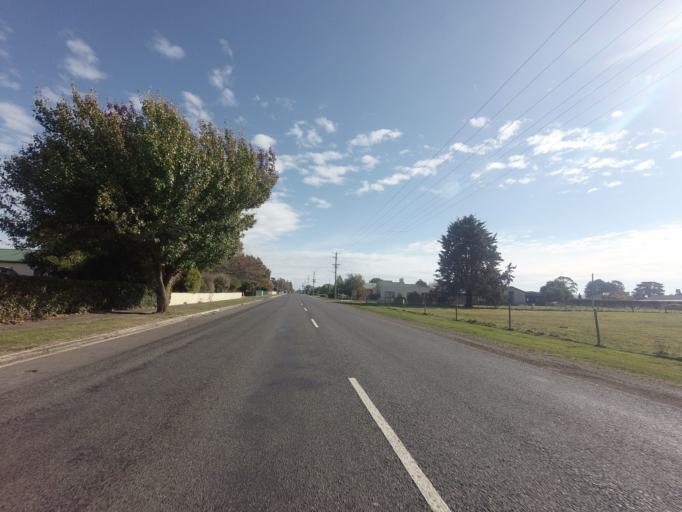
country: AU
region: Tasmania
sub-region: Meander Valley
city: Westbury
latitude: -41.5261
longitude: 146.8477
